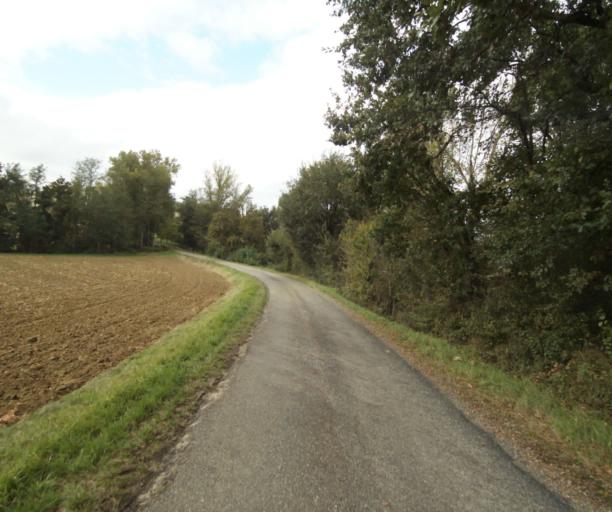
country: FR
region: Midi-Pyrenees
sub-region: Departement du Tarn-et-Garonne
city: Beaumont-de-Lomagne
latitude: 43.8912
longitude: 1.0807
